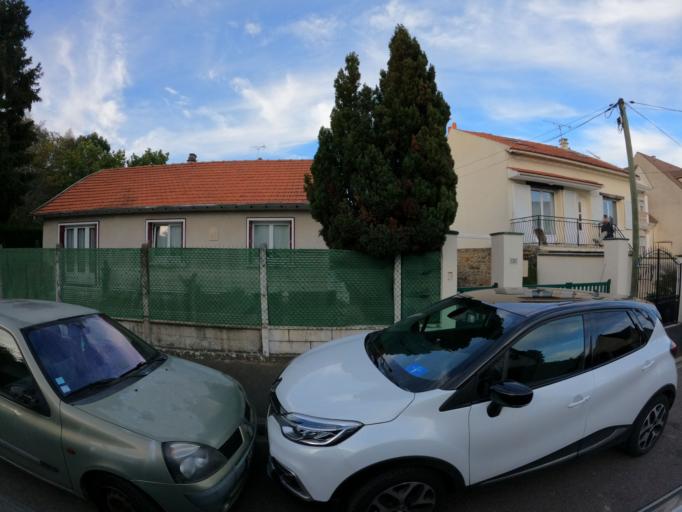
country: FR
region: Ile-de-France
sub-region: Departement de Seine-et-Marne
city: Pontault-Combault
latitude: 48.8104
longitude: 2.5964
